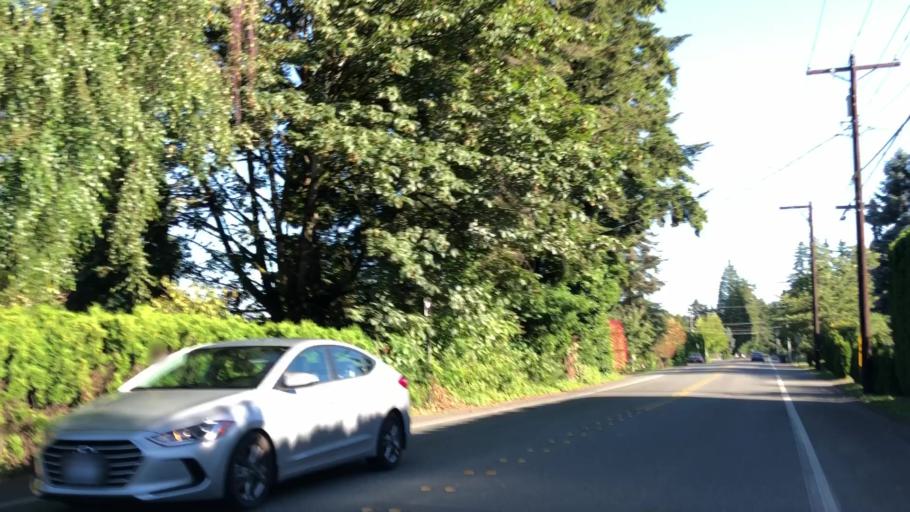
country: US
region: Washington
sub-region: Snohomish County
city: Martha Lake
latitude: 47.8369
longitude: -122.2463
